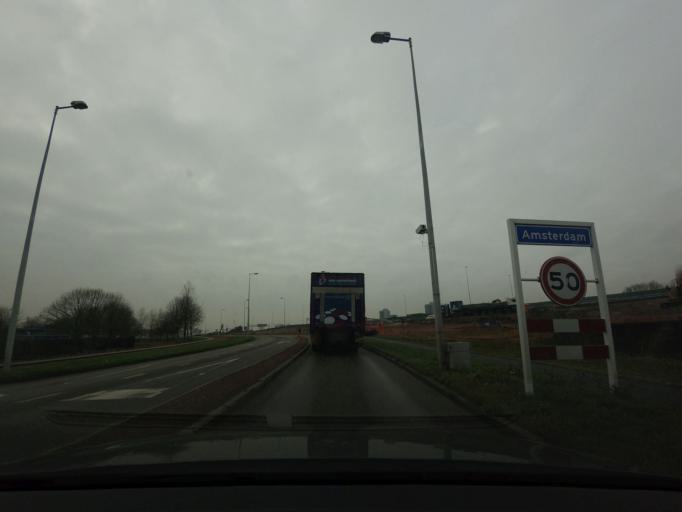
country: NL
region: North Holland
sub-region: Gemeente Amsterdam
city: Amsterdam-Zuidoost
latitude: 52.3154
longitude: 4.9948
